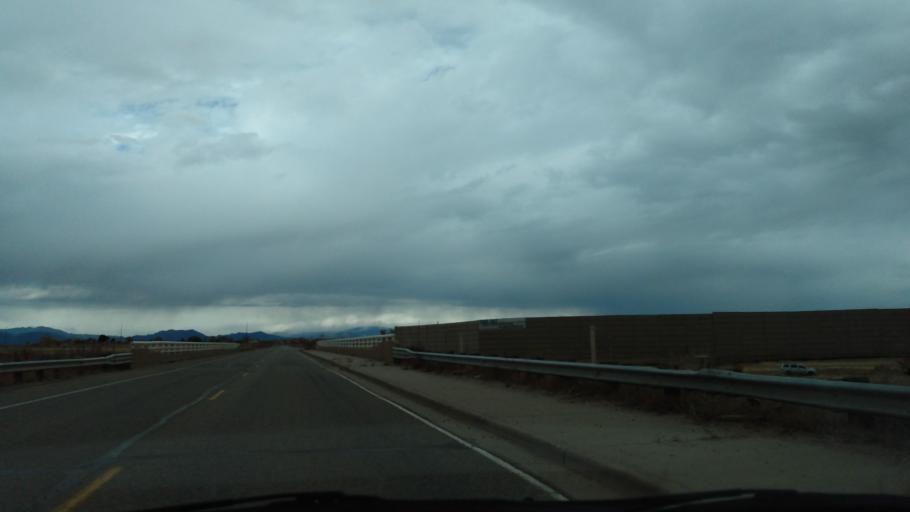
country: US
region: Colorado
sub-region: Adams County
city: Northglenn
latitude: 39.9727
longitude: -104.9648
